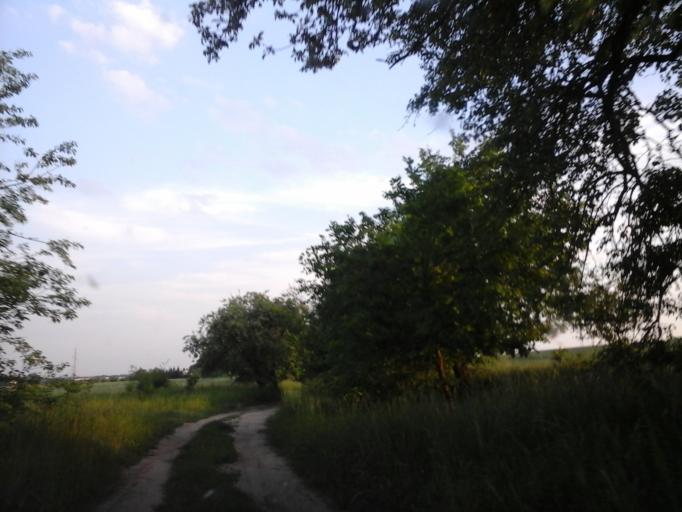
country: PL
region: West Pomeranian Voivodeship
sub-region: Powiat choszczenski
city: Choszczno
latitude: 53.1922
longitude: 15.4174
